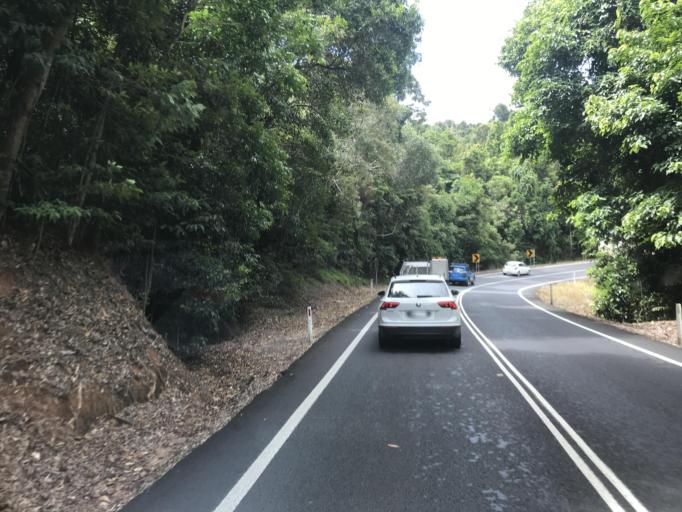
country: AU
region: Queensland
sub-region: Cassowary Coast
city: Innisfail
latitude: -17.8677
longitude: 146.0719
